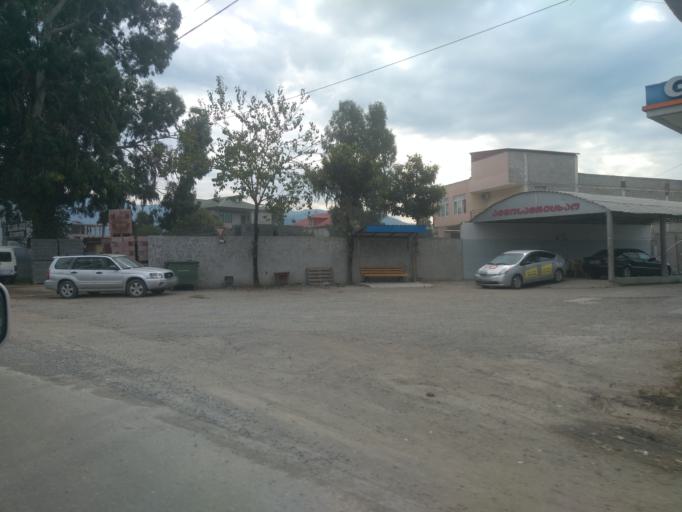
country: GE
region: Ajaria
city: Batumi
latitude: 41.6093
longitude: 41.6259
